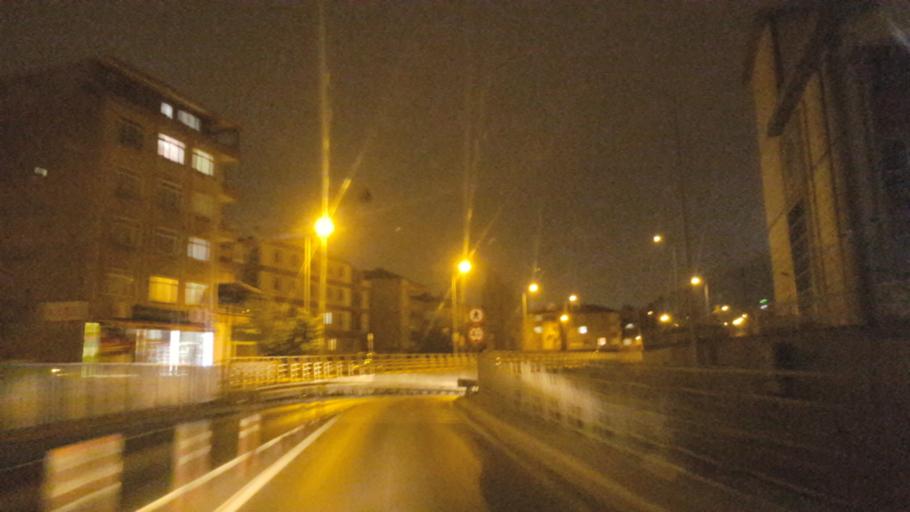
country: TR
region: Kocaeli
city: Darica
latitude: 40.7859
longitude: 29.3995
